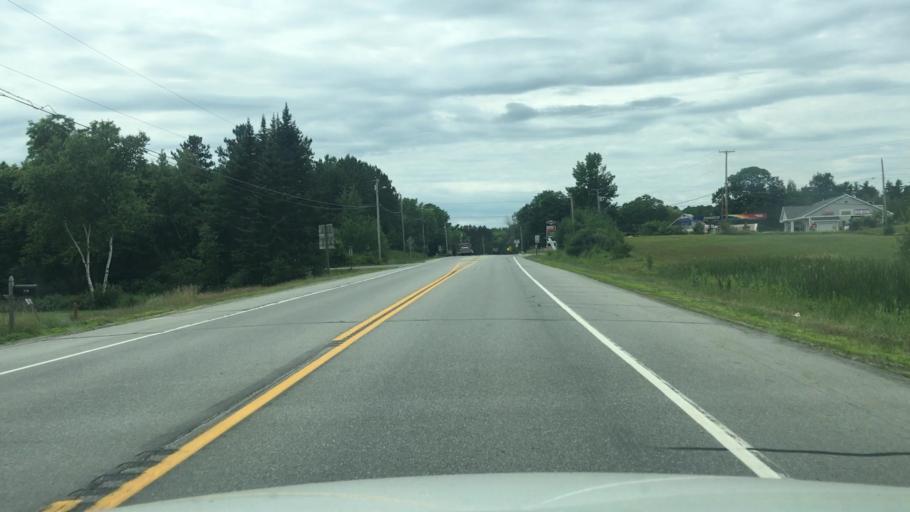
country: US
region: Maine
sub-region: Kennebec County
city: Windsor
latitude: 44.3880
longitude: -69.5922
